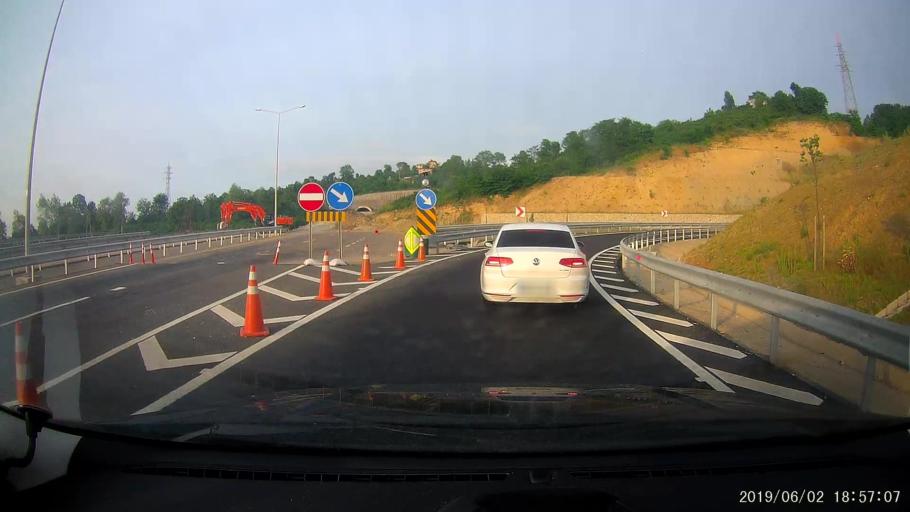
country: TR
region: Ordu
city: Ordu
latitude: 40.9536
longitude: 37.9034
